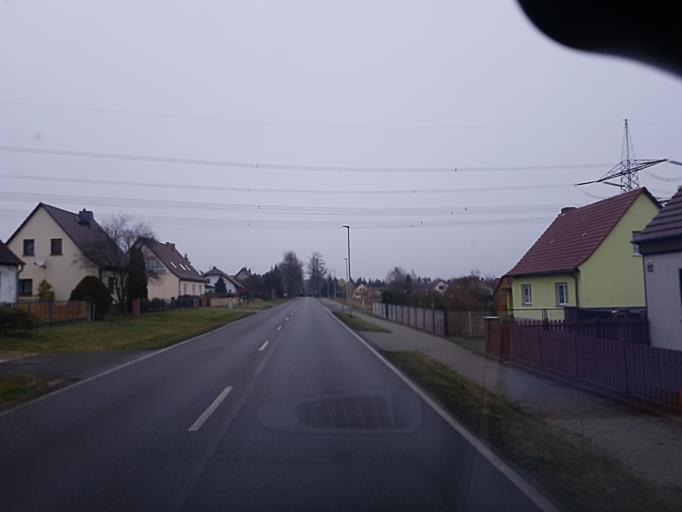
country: DE
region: Brandenburg
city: Lubbenau
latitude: 51.8823
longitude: 13.9054
